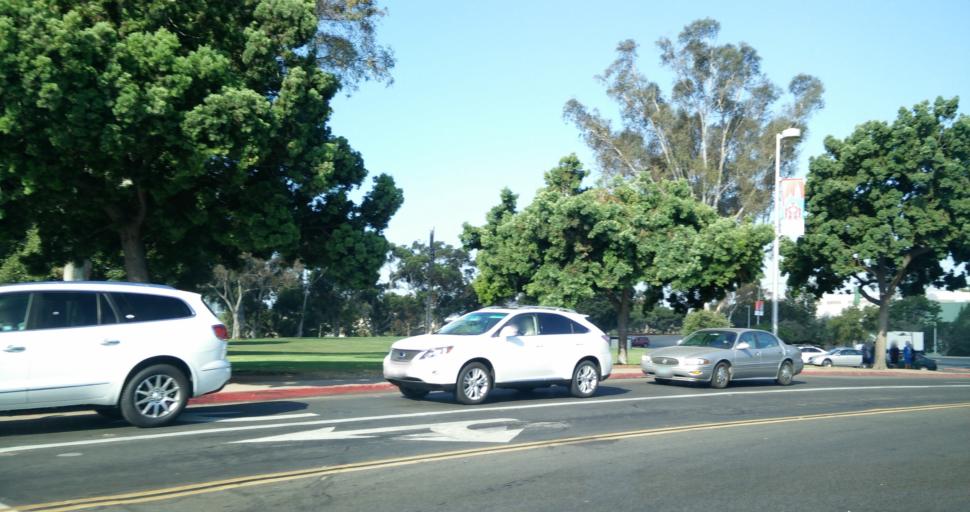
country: US
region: California
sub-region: San Diego County
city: San Diego
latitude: 32.7257
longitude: -117.1507
